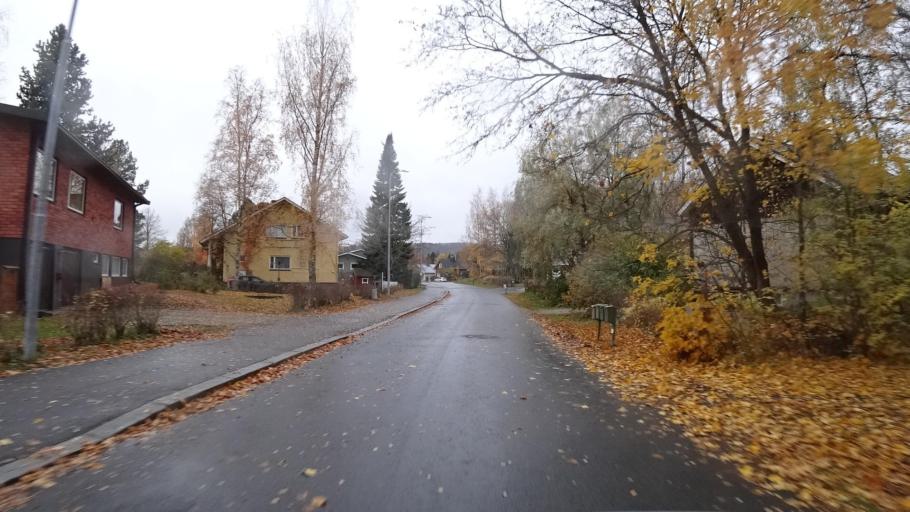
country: FI
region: Northern Savo
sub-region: Kuopio
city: Kuopio
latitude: 62.9257
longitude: 27.6945
